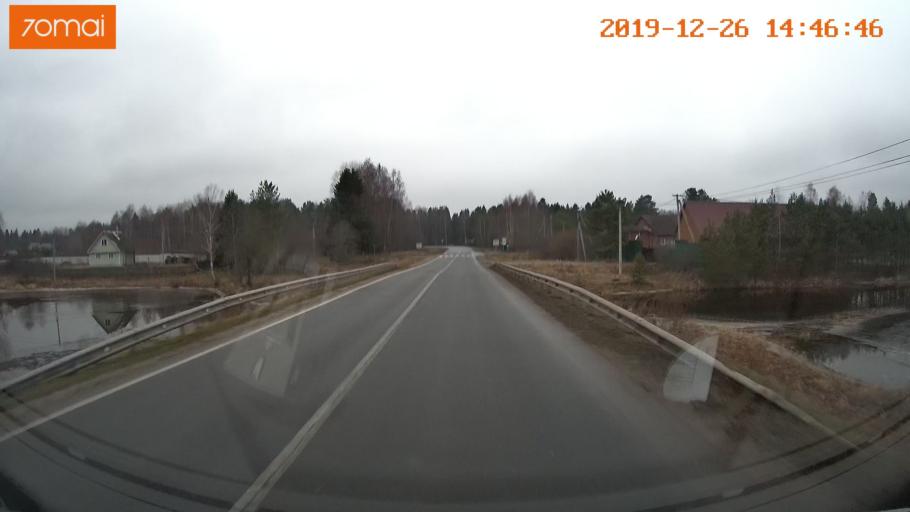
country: RU
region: Jaroslavl
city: Poshekhon'ye
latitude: 58.3392
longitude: 39.0121
